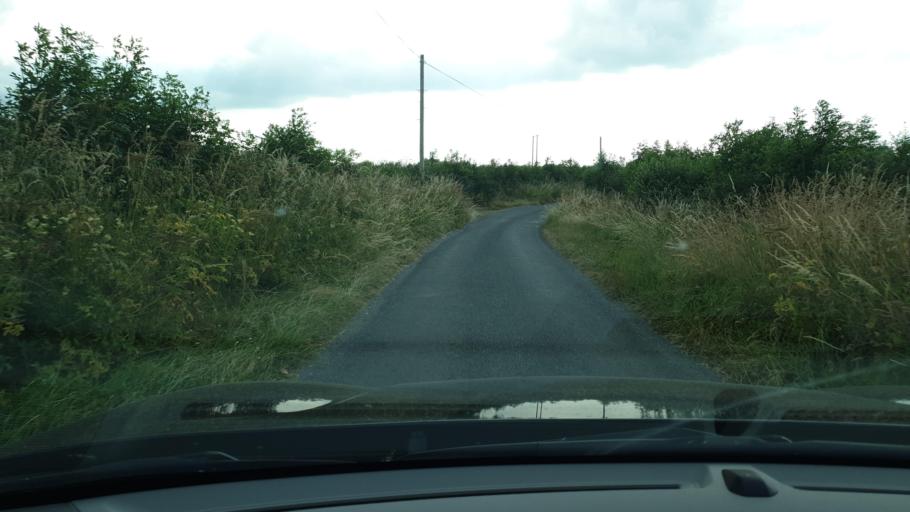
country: IE
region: Leinster
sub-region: An Mhi
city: Ashbourne
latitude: 53.4648
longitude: -6.4262
